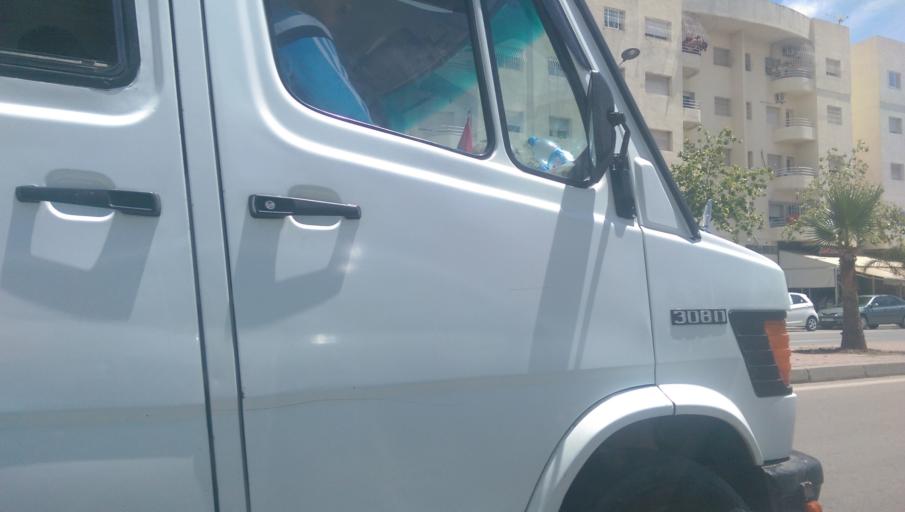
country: MA
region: Fes-Boulemane
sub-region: Fes
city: Fes
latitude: 34.0175
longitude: -4.9853
